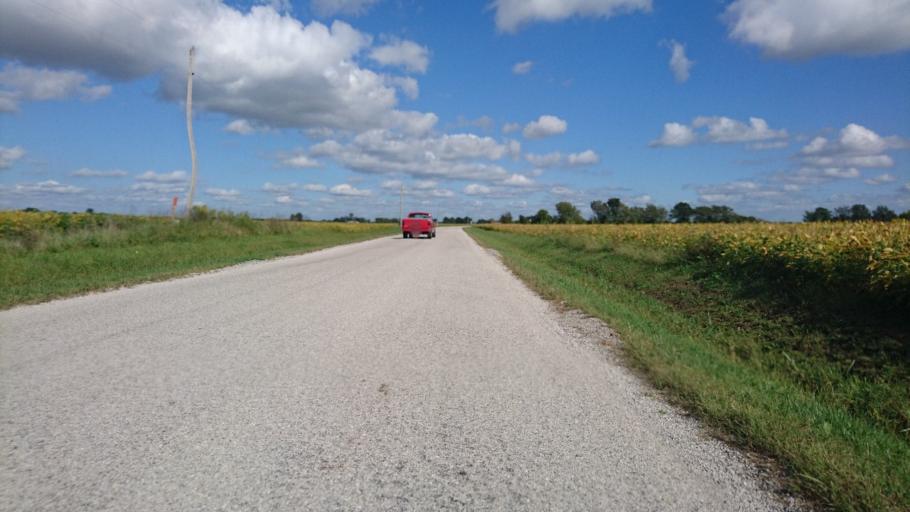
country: US
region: Illinois
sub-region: Macoupin County
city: Staunton
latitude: 39.0211
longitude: -89.7398
